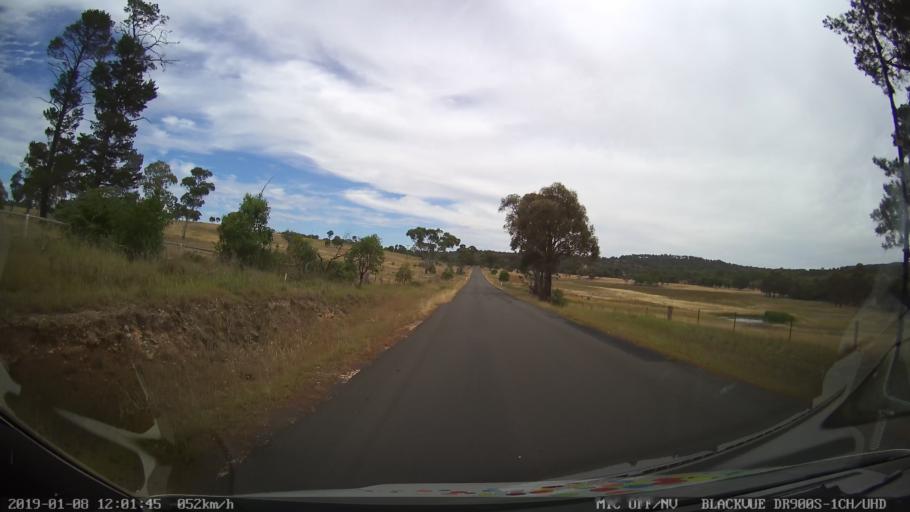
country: AU
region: New South Wales
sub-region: Armidale Dumaresq
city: Armidale
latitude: -30.4595
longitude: 151.6087
